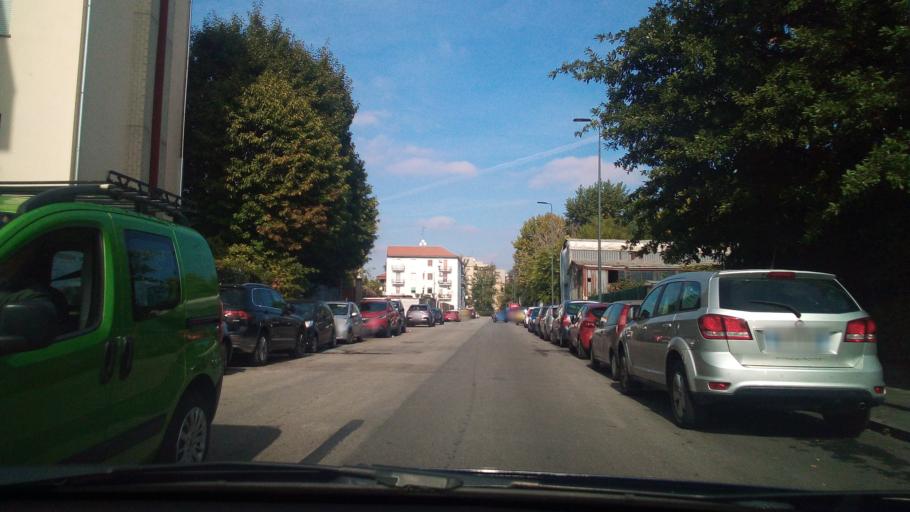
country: IT
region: Lombardy
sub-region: Citta metropolitana di Milano
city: Sesto San Giovanni
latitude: 45.5086
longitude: 9.2305
